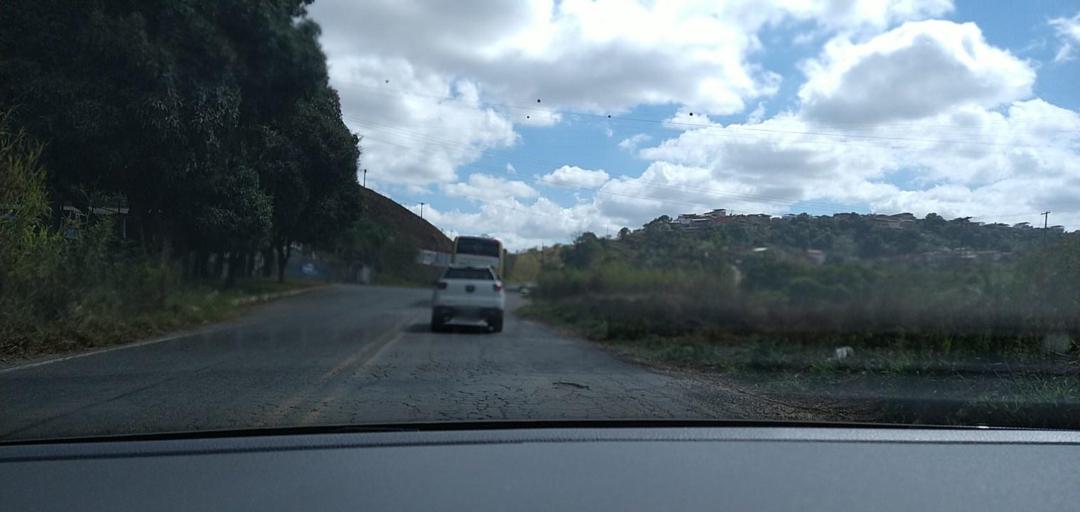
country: BR
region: Minas Gerais
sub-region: Ponte Nova
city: Ponte Nova
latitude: -20.4263
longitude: -42.8942
